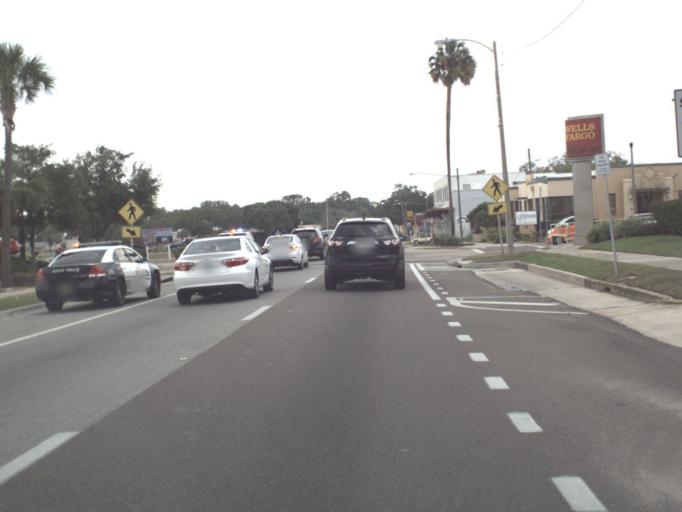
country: US
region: Florida
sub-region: Lake County
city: Eustis
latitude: 28.8532
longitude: -81.6836
